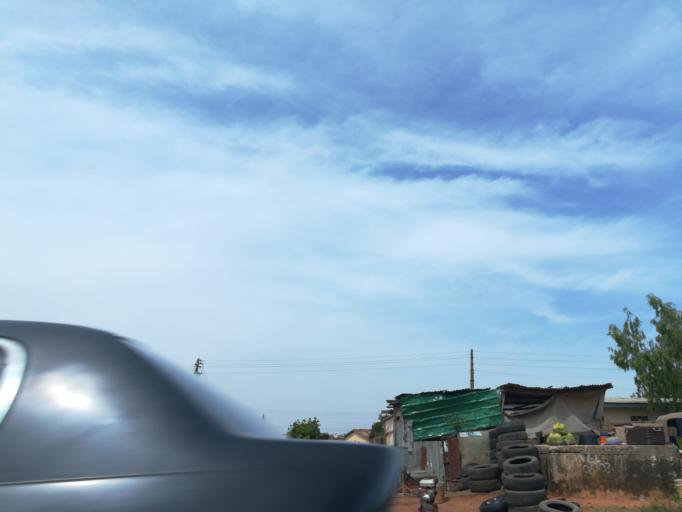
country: NG
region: Plateau
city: Jos
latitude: 9.8743
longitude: 8.8505
